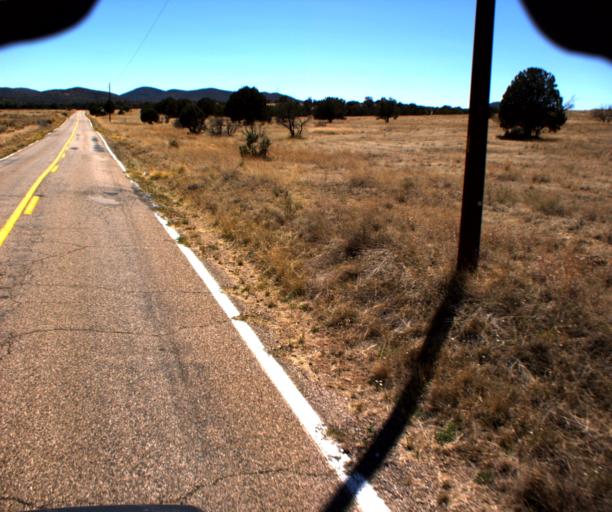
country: US
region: Arizona
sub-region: Cochise County
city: Huachuca City
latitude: 31.5485
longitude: -110.5293
